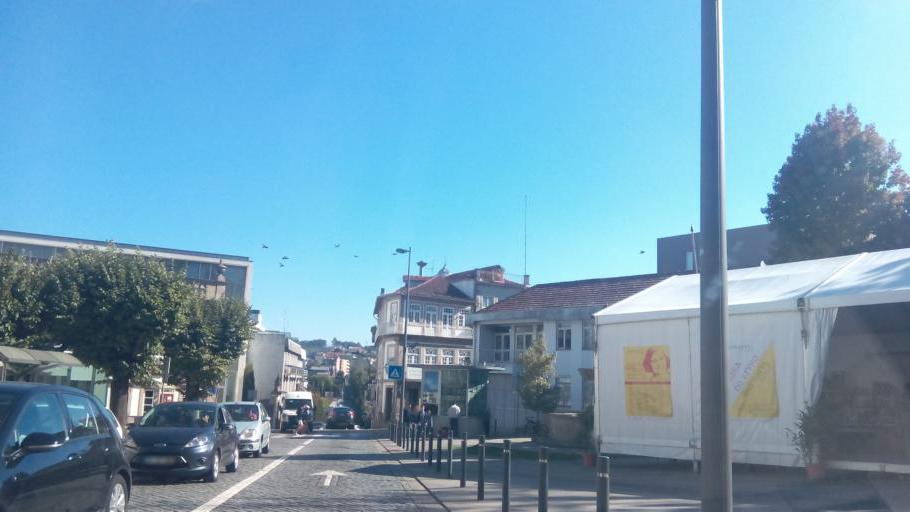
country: PT
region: Porto
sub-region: Penafiel
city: Penafiel
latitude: 41.2073
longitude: -8.2848
